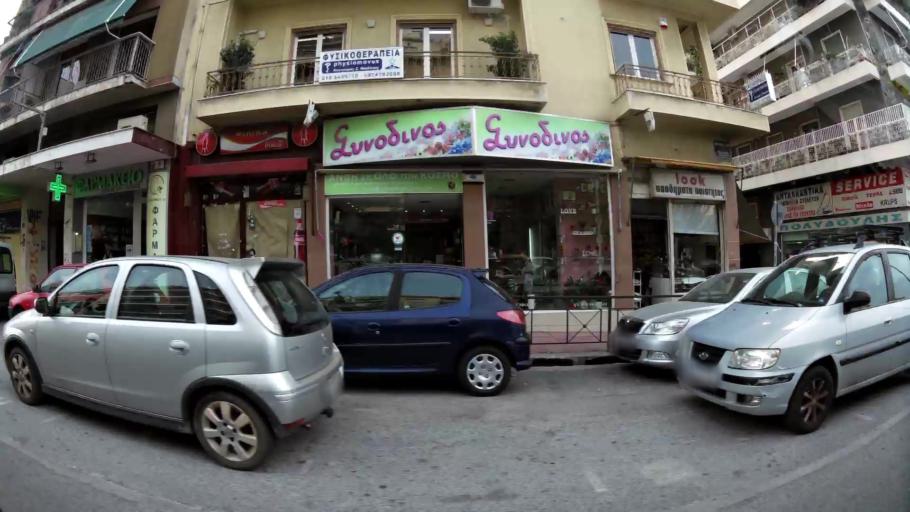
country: GR
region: Attica
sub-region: Nomarchia Athinas
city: Kipseli
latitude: 37.9885
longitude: 23.7582
